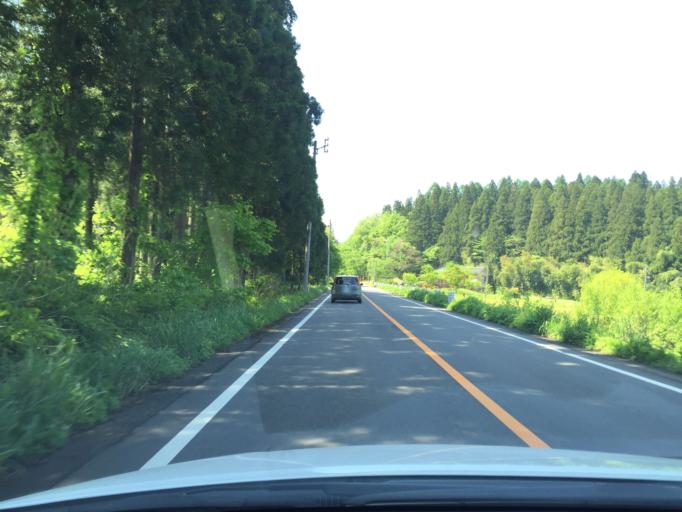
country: JP
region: Niigata
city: Muramatsu
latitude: 37.6577
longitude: 139.1378
